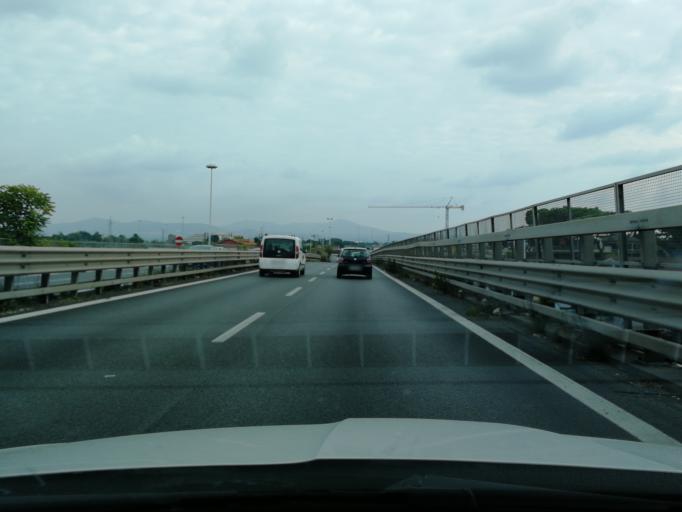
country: IT
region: Latium
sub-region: Citta metropolitana di Roma Capitale
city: Ciampino
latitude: 41.8422
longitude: 12.5850
